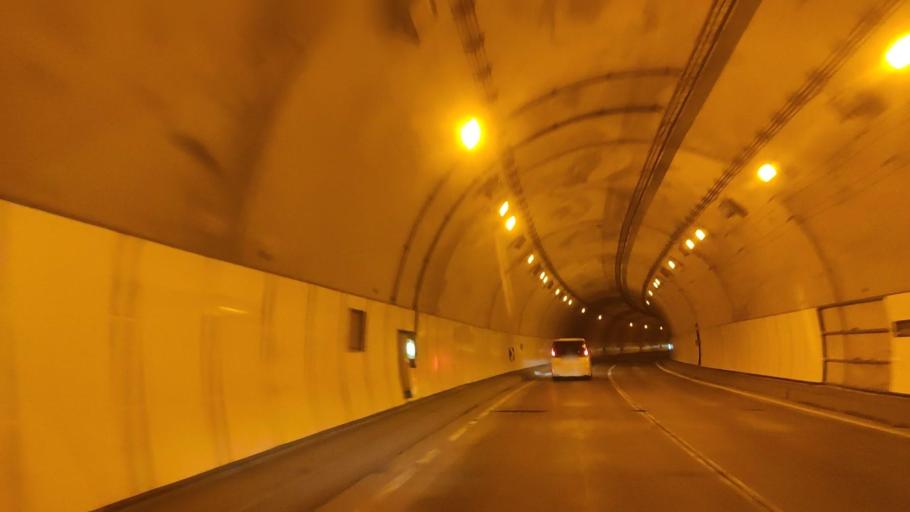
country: JP
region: Hokkaido
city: Ashibetsu
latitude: 43.3782
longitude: 142.2169
